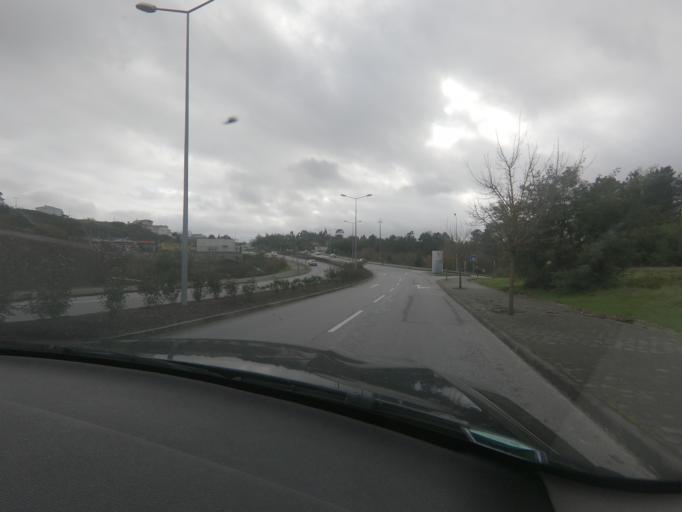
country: PT
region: Viseu
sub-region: Viseu
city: Abraveses
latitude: 40.6821
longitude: -7.9274
